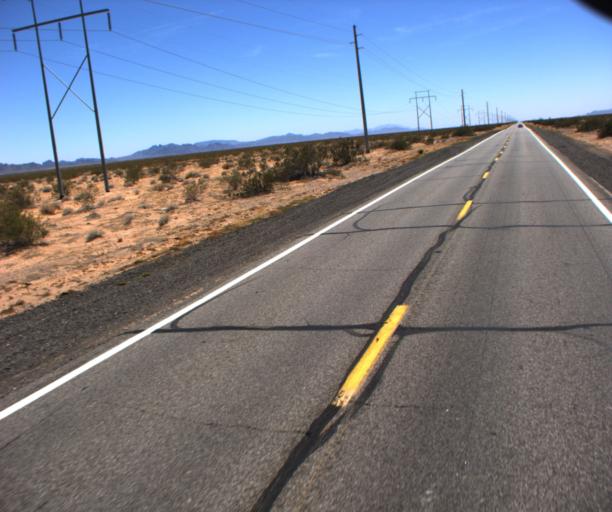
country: US
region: Arizona
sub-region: La Paz County
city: Quartzsite
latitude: 33.9066
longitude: -114.2169
